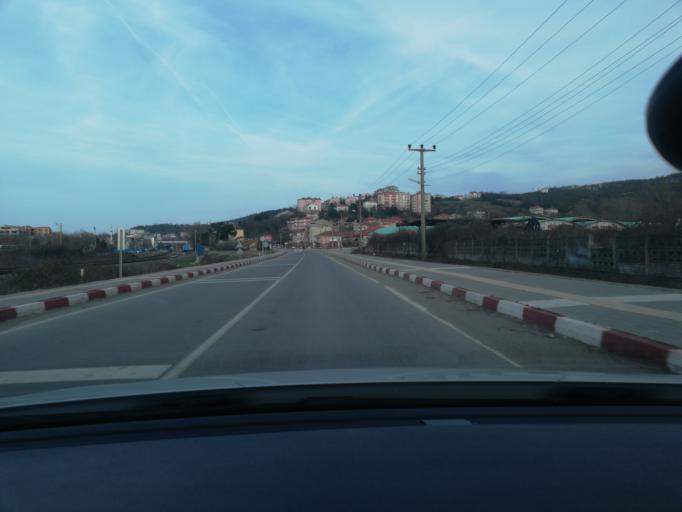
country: TR
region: Zonguldak
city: Tieum
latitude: 41.5576
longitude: 32.0160
